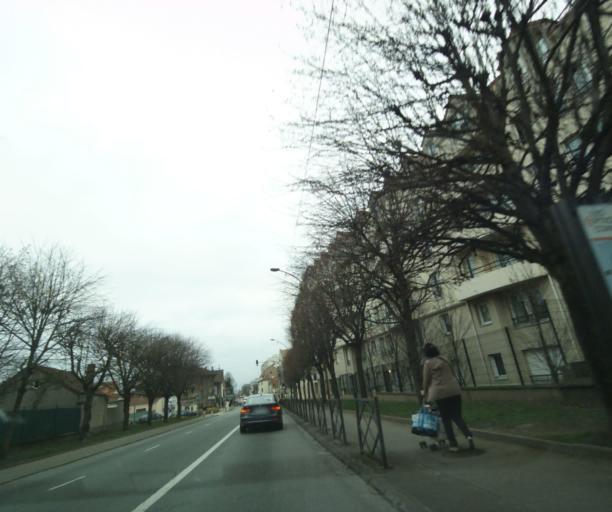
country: FR
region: Ile-de-France
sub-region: Departement des Yvelines
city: Poissy
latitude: 48.9278
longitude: 2.0498
